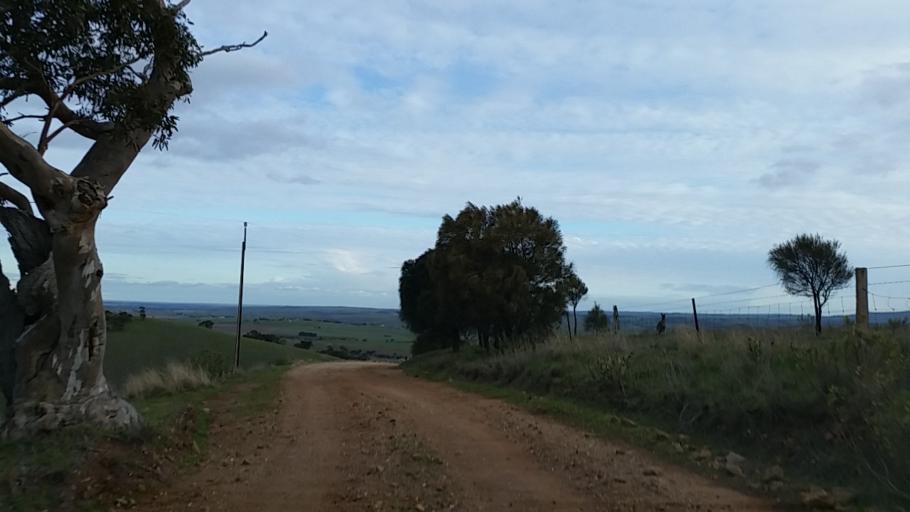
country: AU
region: South Australia
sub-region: Mount Barker
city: Callington
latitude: -34.9994
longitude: 139.0547
